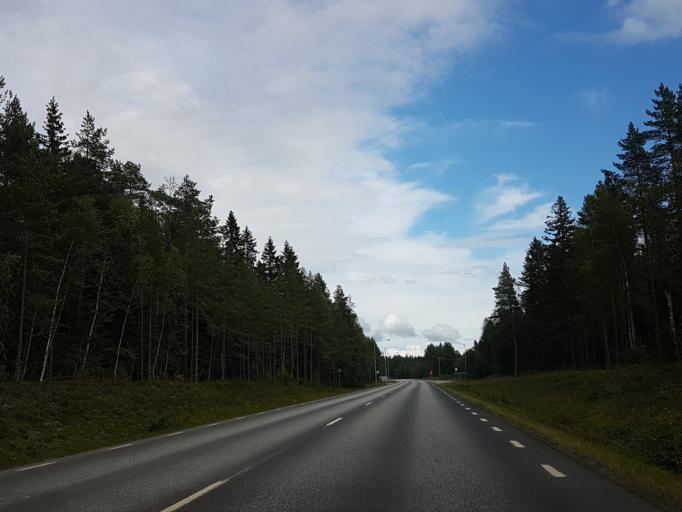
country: SE
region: Vaesterbotten
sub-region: Umea Kommun
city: Taftea
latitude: 63.8159
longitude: 20.4185
